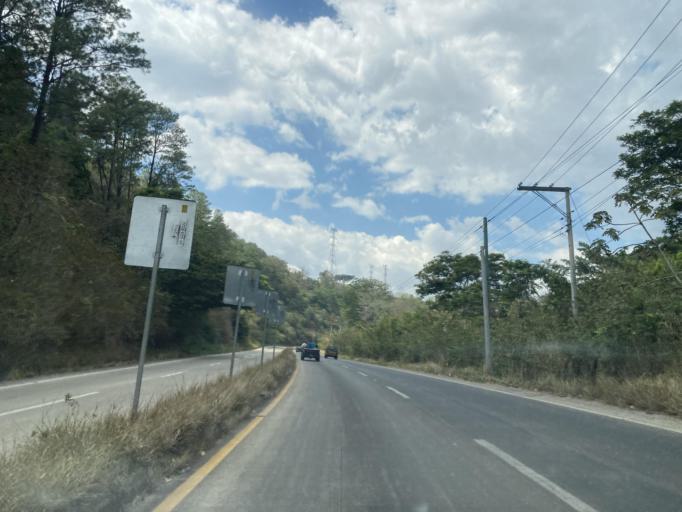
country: GT
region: Santa Rosa
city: Barberena
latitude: 14.3397
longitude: -90.4445
